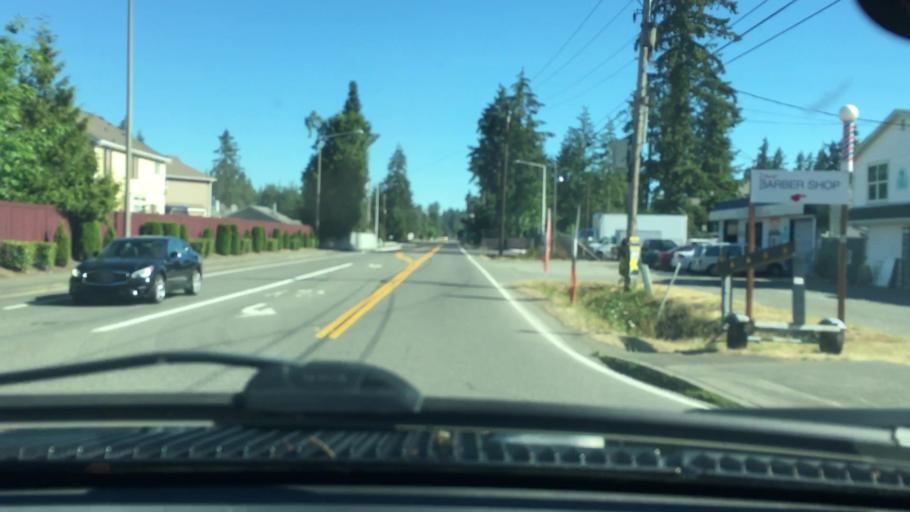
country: US
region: Washington
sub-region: King County
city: Covington
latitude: 47.3510
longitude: -122.1389
